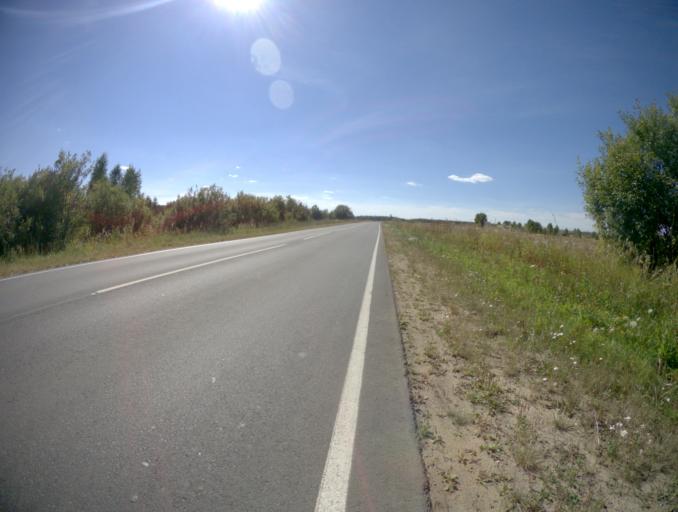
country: RU
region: Vladimir
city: Anopino
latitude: 55.6361
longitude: 40.8118
